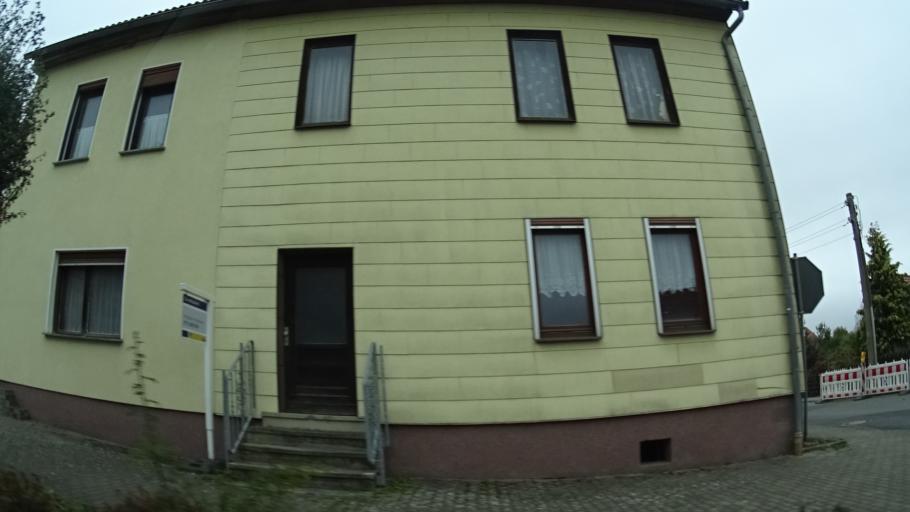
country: DE
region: Thuringia
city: Kaltensundheim
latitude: 50.6050
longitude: 10.1577
